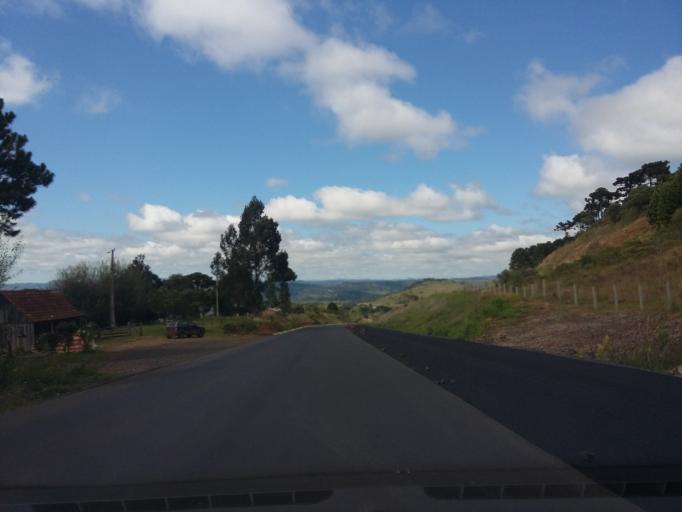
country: BR
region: Santa Catarina
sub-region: Sao Joaquim
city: Sao Joaquim
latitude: -28.0622
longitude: -50.0735
